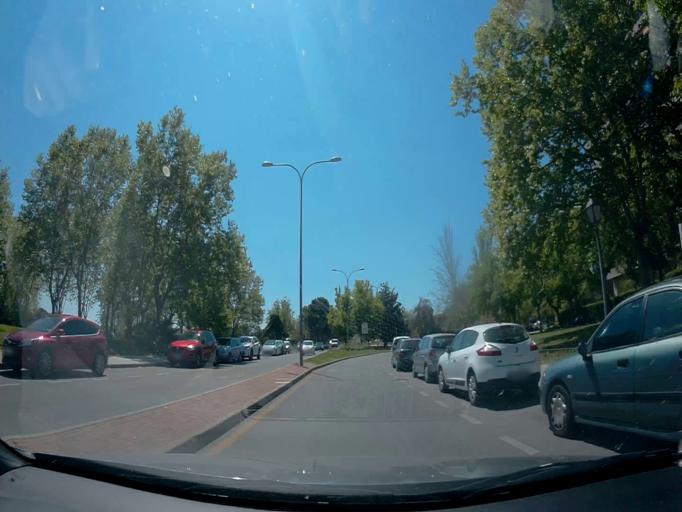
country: ES
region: Madrid
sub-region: Provincia de Madrid
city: Alcorcon
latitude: 40.3404
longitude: -3.8170
